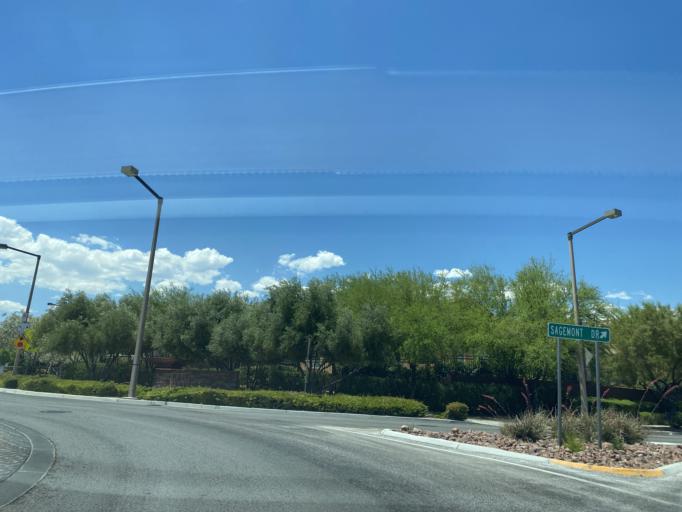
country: US
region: Nevada
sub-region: Clark County
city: Summerlin South
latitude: 36.1539
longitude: -115.3402
